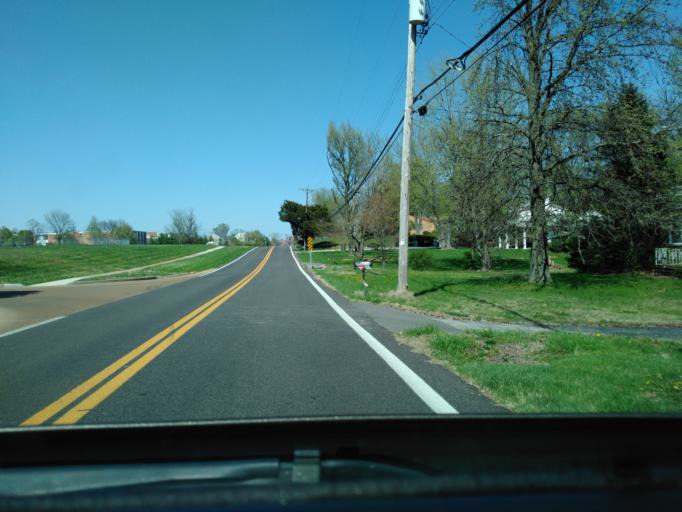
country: US
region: Missouri
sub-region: Saint Louis County
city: Concord
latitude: 38.4918
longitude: -90.3698
